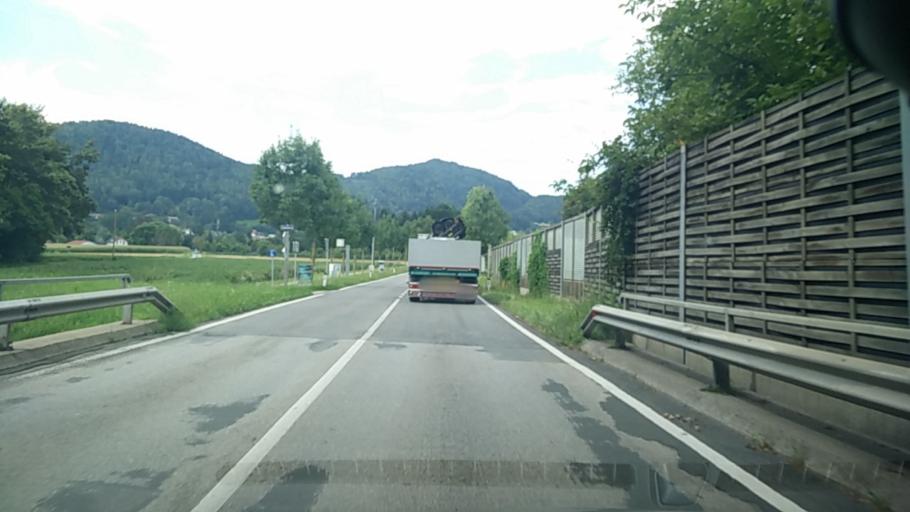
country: AT
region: Carinthia
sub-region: Klagenfurt am Woerthersee
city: Klagenfurt am Woerthersee
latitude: 46.6085
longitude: 14.2715
